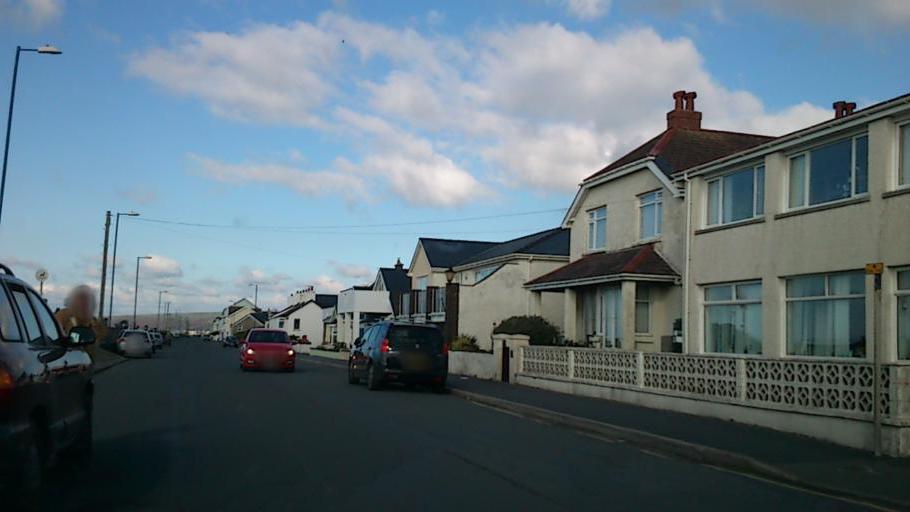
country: GB
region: Wales
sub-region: County of Ceredigion
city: Bow Street
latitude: 52.4914
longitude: -4.0515
